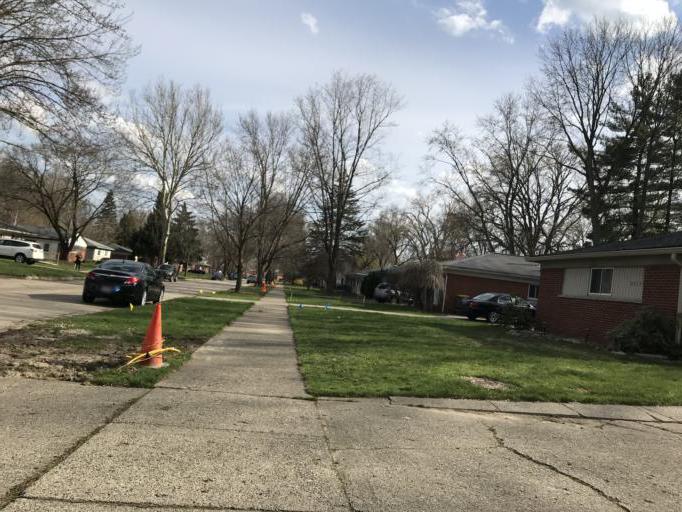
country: US
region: Michigan
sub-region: Oakland County
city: Farmington
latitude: 42.4615
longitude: -83.3471
